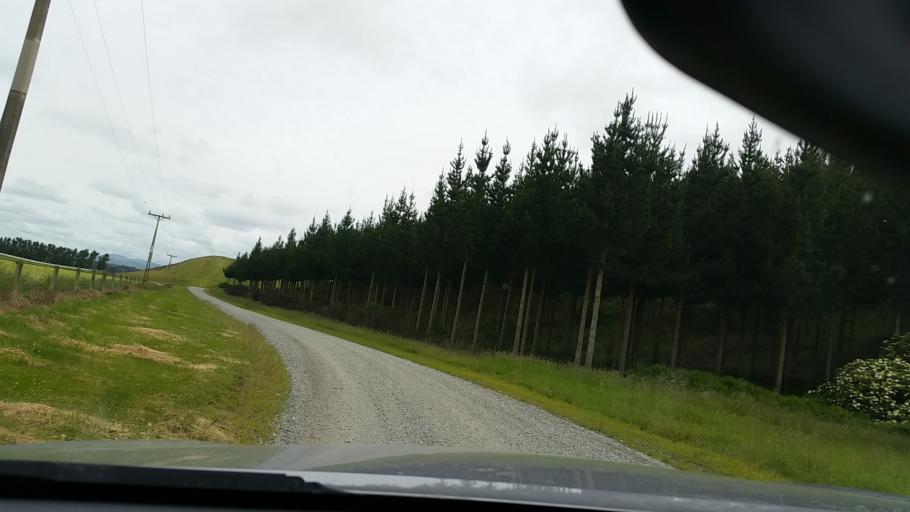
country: NZ
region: Southland
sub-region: Gore District
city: Gore
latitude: -45.8299
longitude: 168.7391
